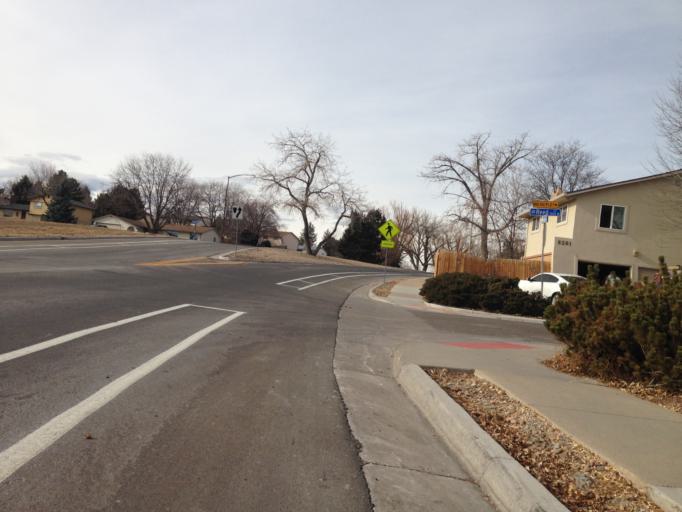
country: US
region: Colorado
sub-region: Adams County
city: Westminster
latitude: 39.8451
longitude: -105.0760
